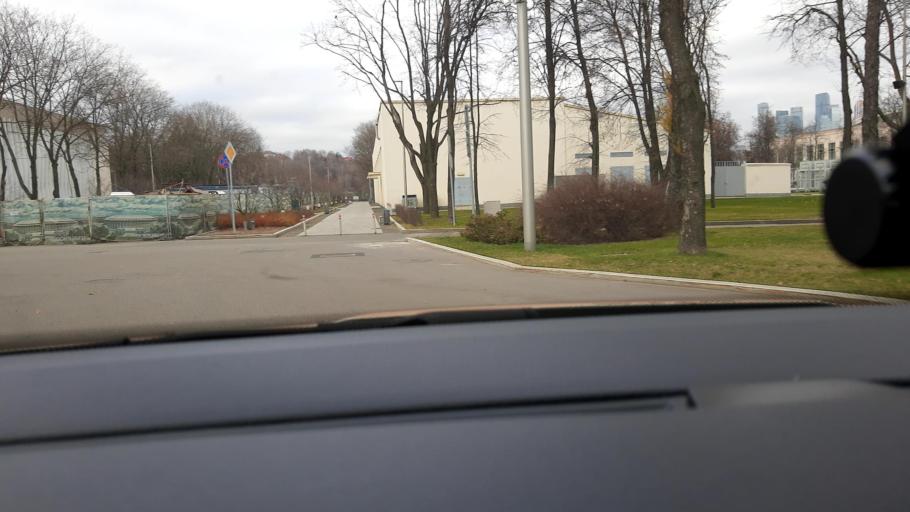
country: RU
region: Moscow
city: Luzhniki
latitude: 55.7195
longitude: 37.5474
